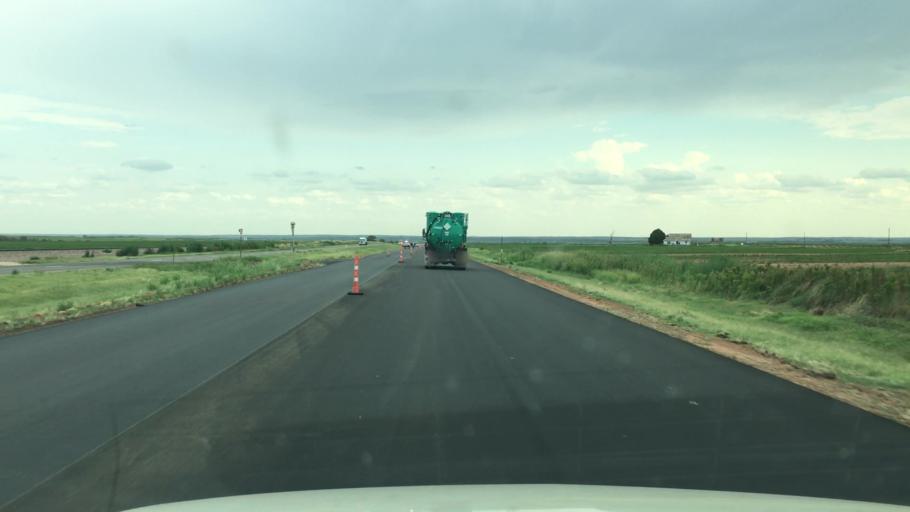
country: US
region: Texas
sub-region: Hall County
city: Memphis
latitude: 34.6184
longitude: -100.4715
